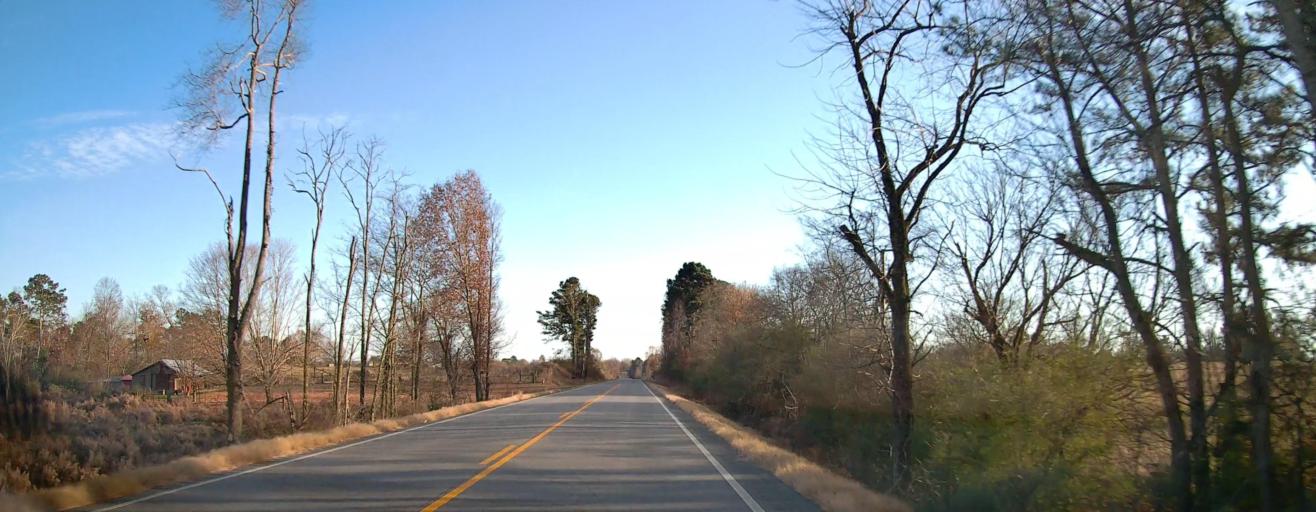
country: US
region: Alabama
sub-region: Marshall County
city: Arab
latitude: 34.2572
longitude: -86.5715
